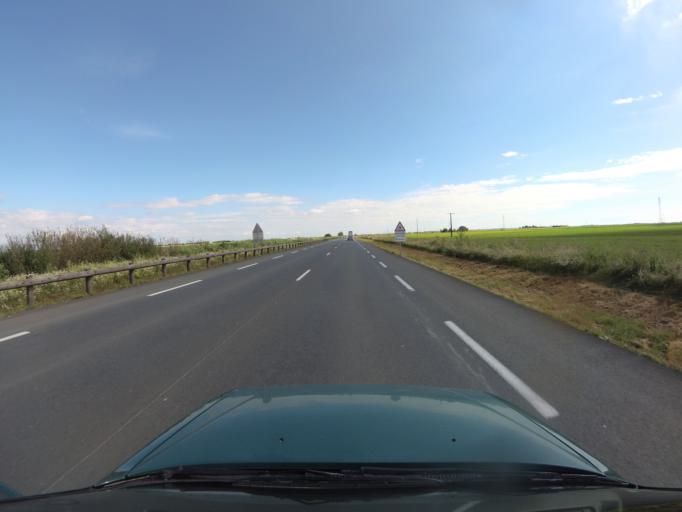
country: FR
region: Pays de la Loire
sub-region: Departement de la Vendee
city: Champagne-les-Marais
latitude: 46.3481
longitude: -1.0848
